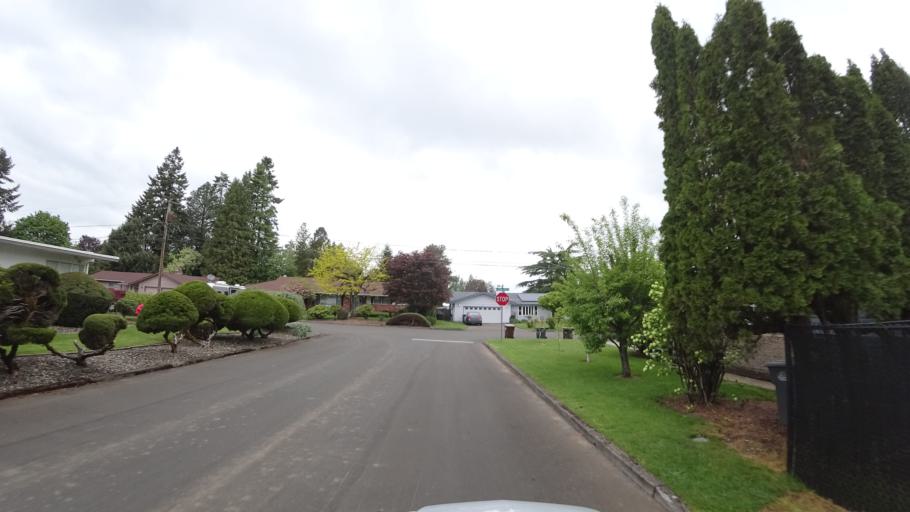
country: US
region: Oregon
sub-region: Washington County
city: Hillsboro
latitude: 45.5290
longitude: -122.9785
